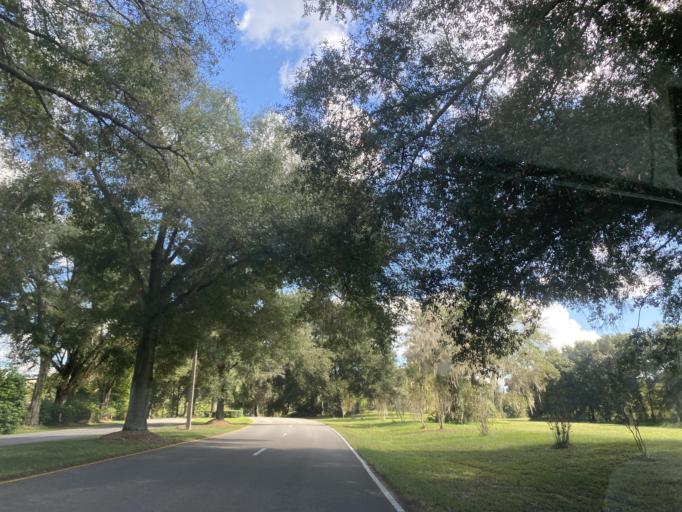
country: US
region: Florida
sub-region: Marion County
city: Ocala
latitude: 29.0604
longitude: -82.2717
